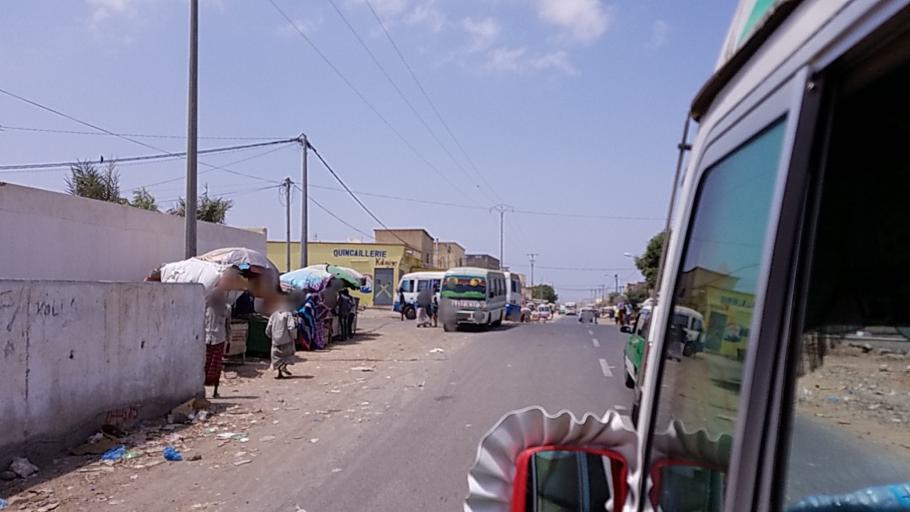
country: DJ
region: Djibouti
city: Djibouti
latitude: 11.5549
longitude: 43.1016
